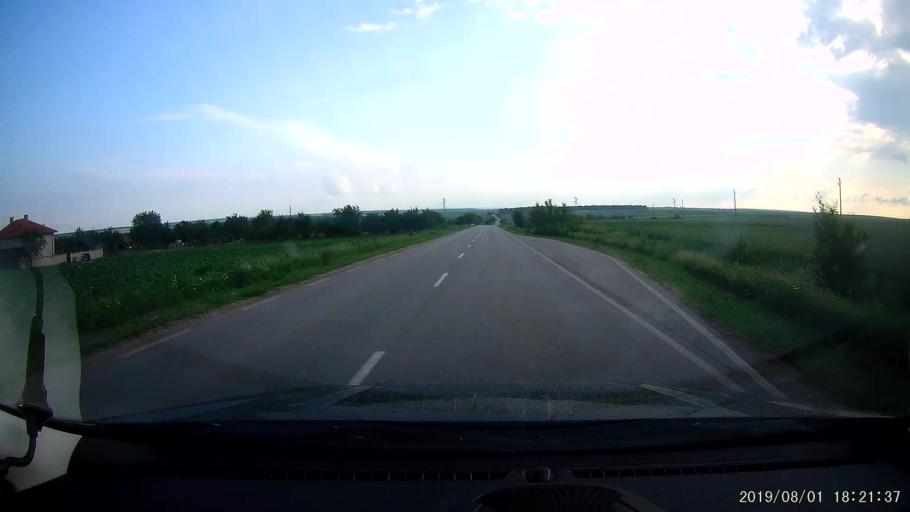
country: BG
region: Shumen
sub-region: Obshtina Kaolinovo
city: Kaolinovo
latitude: 43.6507
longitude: 27.0690
